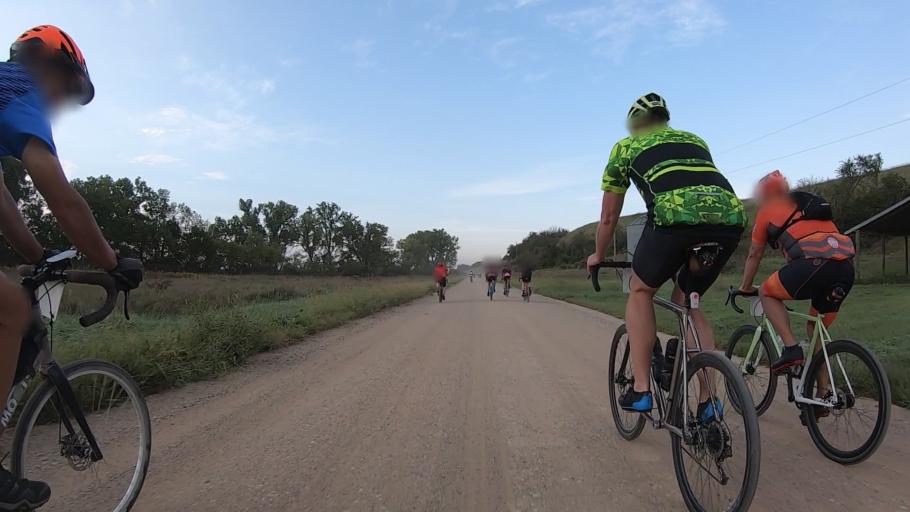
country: US
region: Kansas
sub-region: Marshall County
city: Marysville
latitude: 39.8300
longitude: -96.6648
